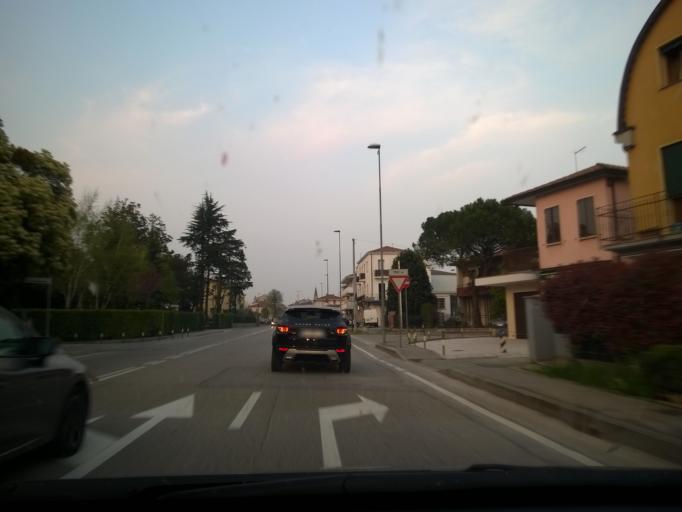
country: IT
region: Veneto
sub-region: Provincia di Padova
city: Noventa
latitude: 45.4225
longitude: 11.9397
